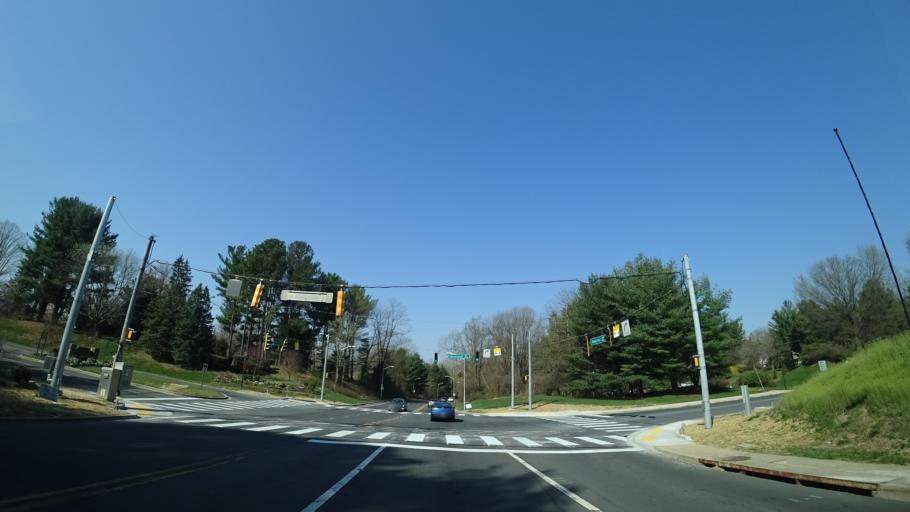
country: US
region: Maryland
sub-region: Montgomery County
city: Potomac
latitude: 39.0224
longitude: -77.1674
